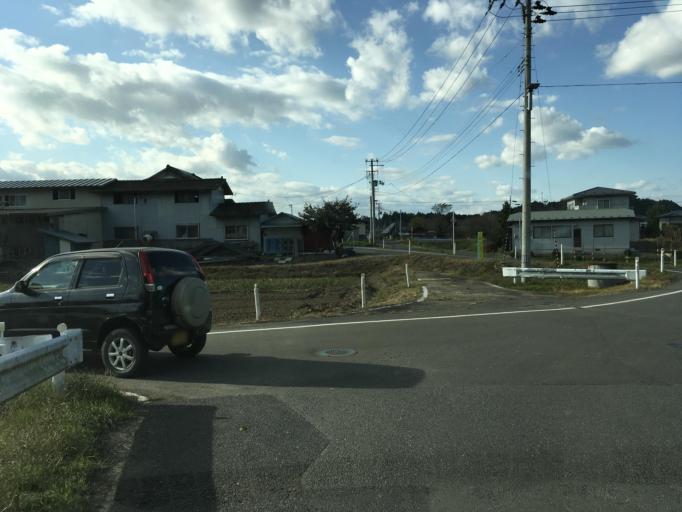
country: JP
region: Miyagi
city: Wakuya
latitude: 38.6514
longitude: 141.2914
